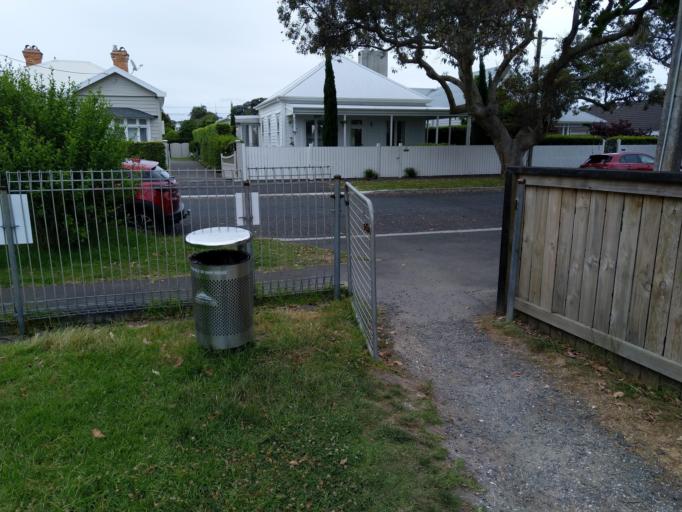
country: NZ
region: Auckland
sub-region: Auckland
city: Auckland
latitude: -36.8238
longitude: 174.8080
